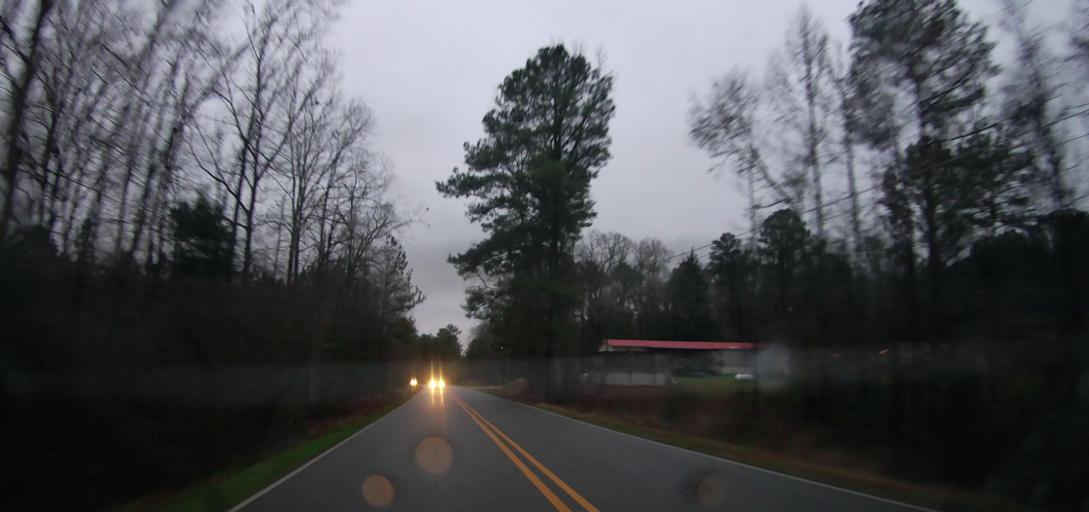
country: US
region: Alabama
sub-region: Tuscaloosa County
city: Vance
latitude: 33.1308
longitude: -87.2298
